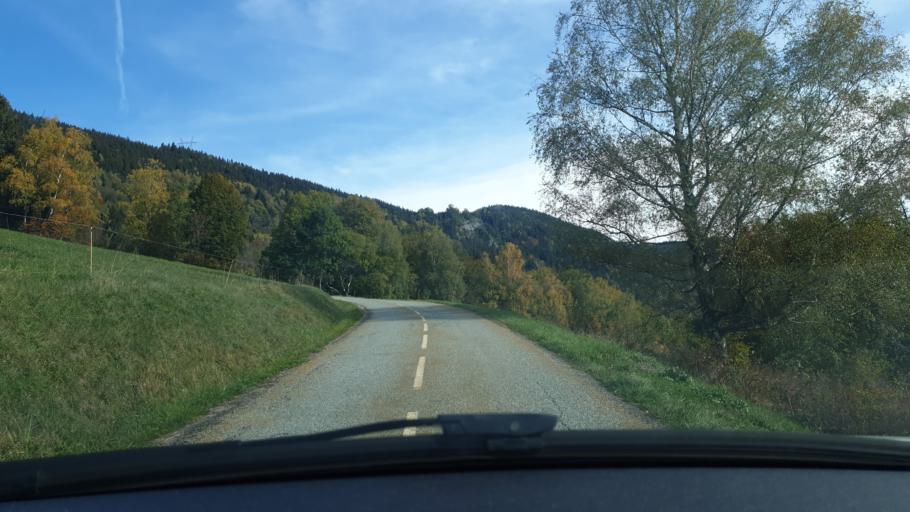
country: FR
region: Rhone-Alpes
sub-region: Departement de la Savoie
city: Aiton
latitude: 45.5011
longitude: 6.2252
